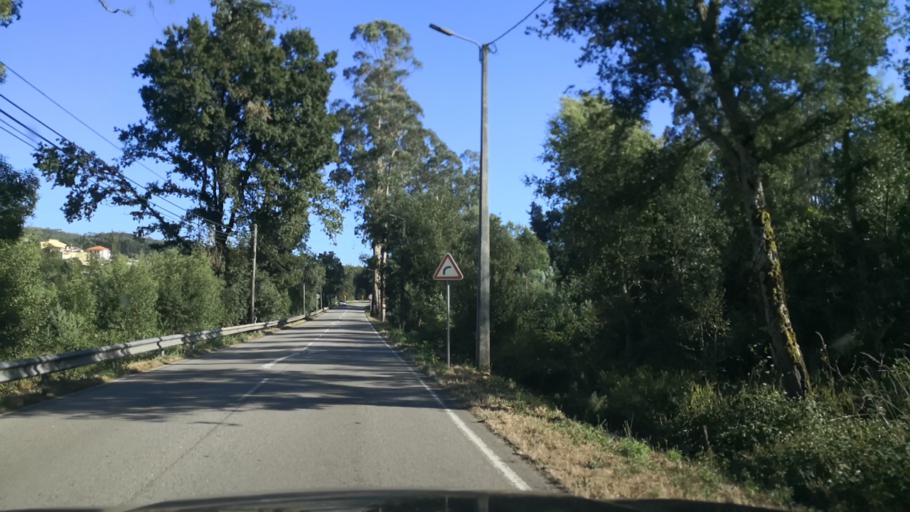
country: PT
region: Porto
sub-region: Pacos de Ferreira
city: Seroa
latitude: 41.2768
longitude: -8.4691
